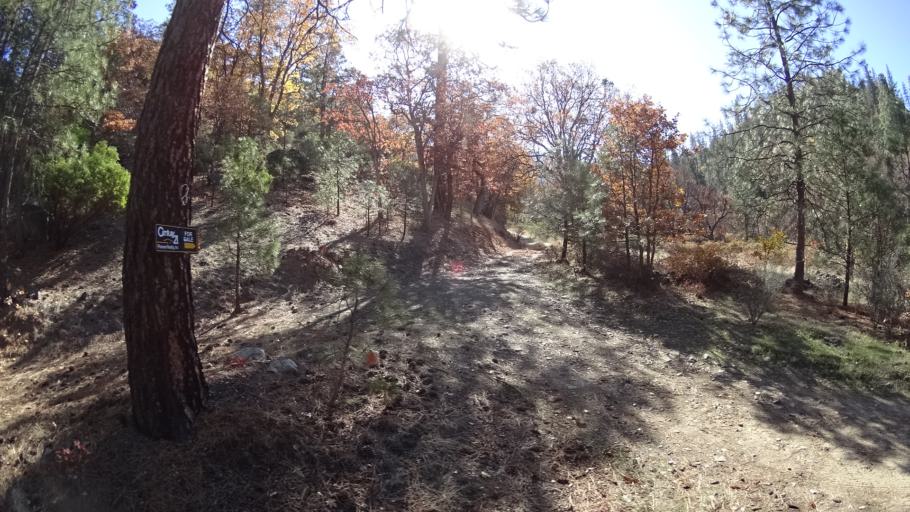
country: US
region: California
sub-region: Siskiyou County
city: Yreka
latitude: 41.8555
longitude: -122.7606
